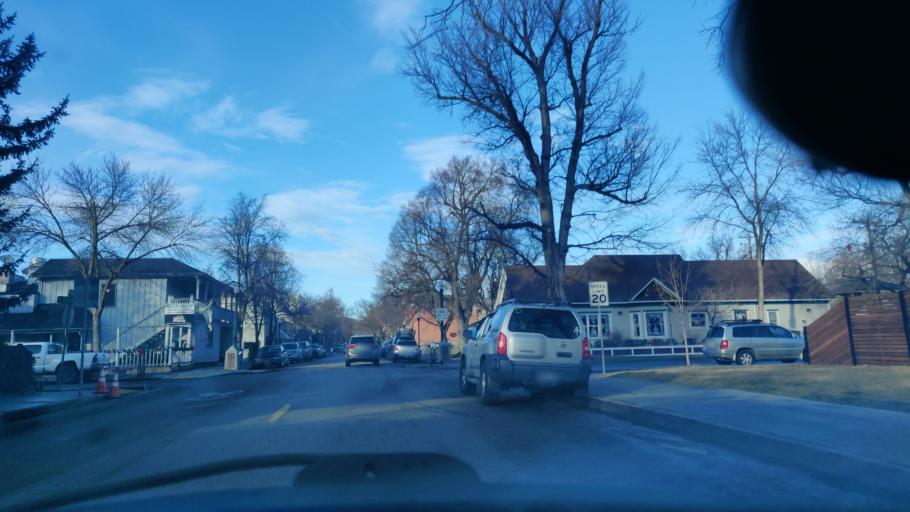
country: US
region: Idaho
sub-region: Ada County
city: Boise
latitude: 43.6290
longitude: -116.2034
